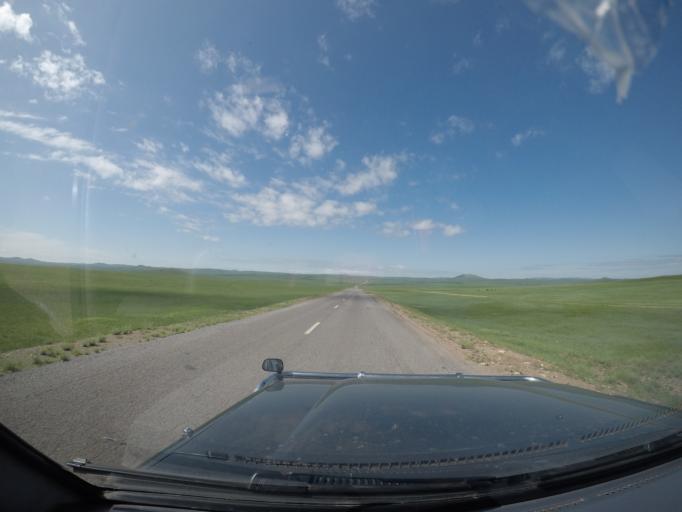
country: MN
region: Suhbaatar
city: Hanhohiy
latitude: 47.3781
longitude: 111.7990
